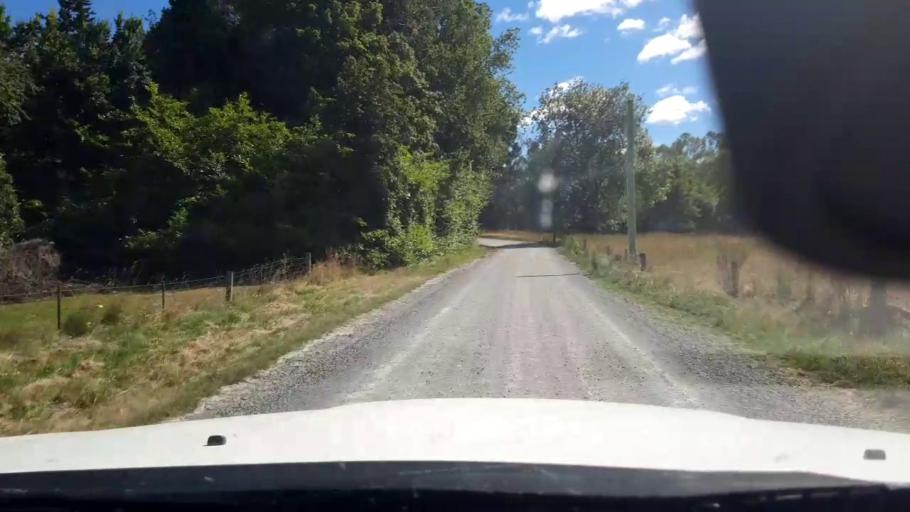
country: NZ
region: Canterbury
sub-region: Timaru District
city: Pleasant Point
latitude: -44.0307
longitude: 170.7432
